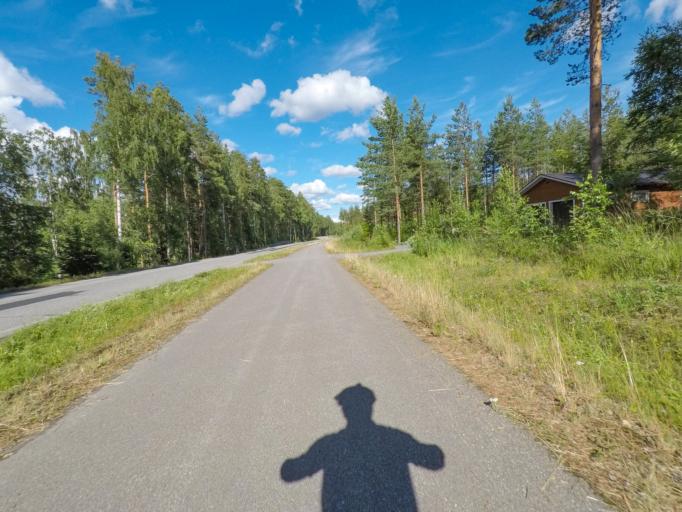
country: FI
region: South Karelia
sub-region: Lappeenranta
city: Joutseno
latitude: 61.1518
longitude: 28.5633
